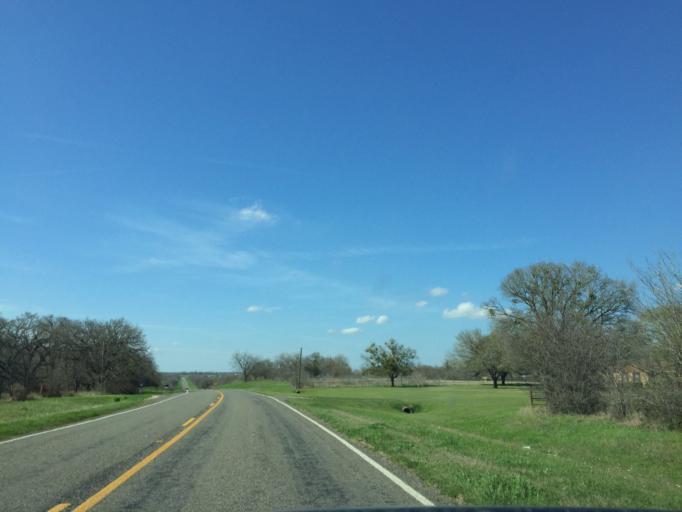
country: US
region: Texas
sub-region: Milam County
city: Thorndale
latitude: 30.5821
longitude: -97.1865
